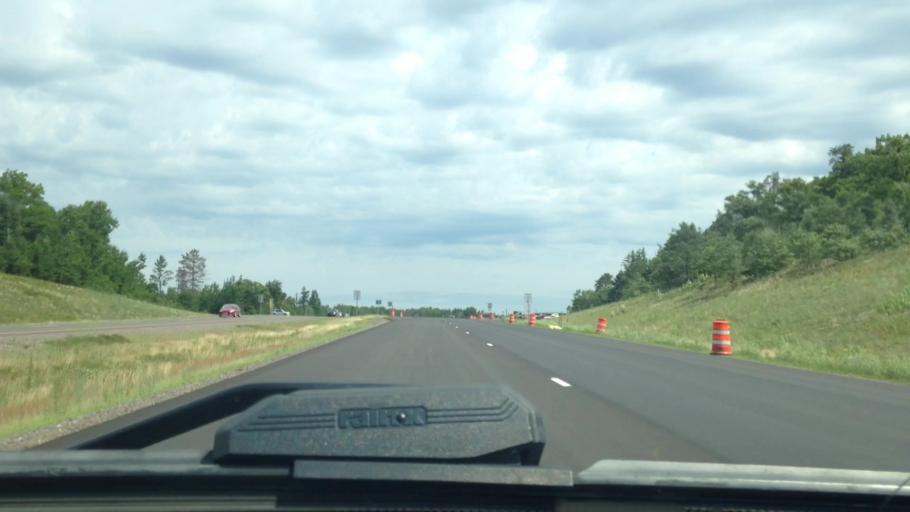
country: US
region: Wisconsin
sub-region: Sawyer County
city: Hayward
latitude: 46.1726
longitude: -91.8045
